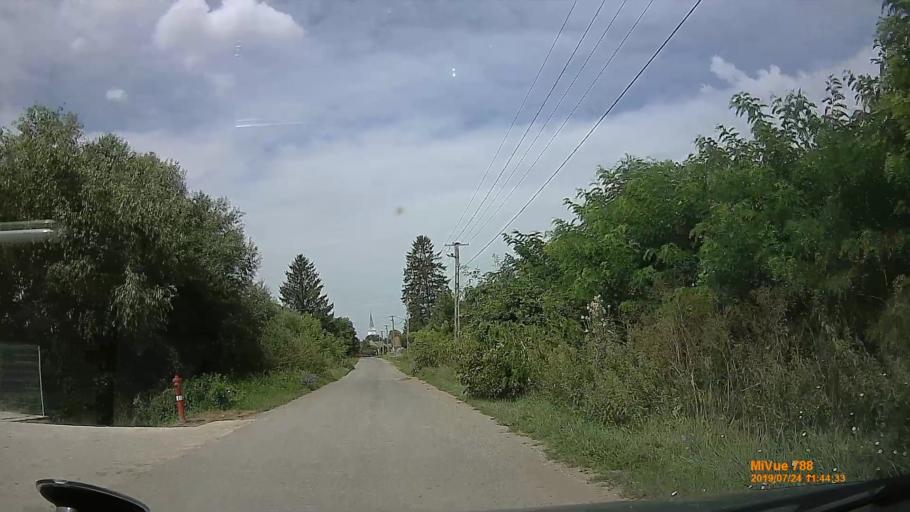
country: UA
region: Zakarpattia
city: Batiovo
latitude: 48.2304
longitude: 22.4407
